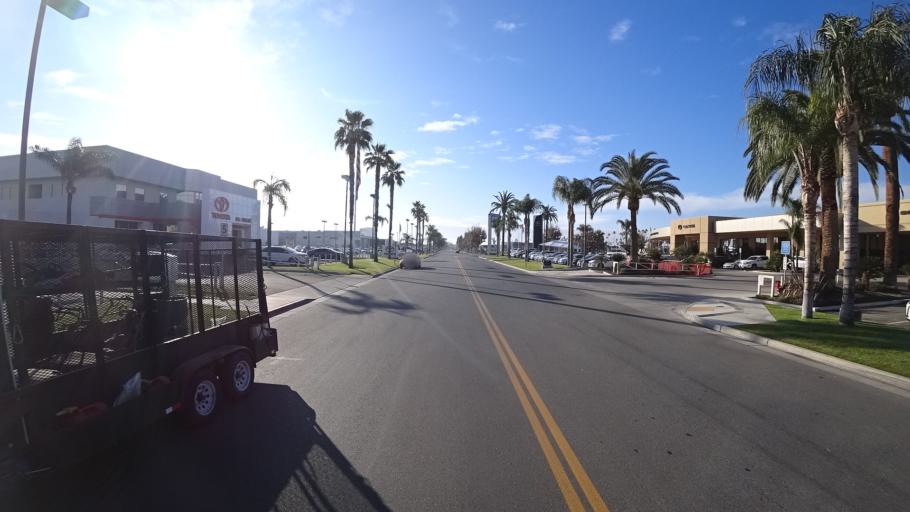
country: US
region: California
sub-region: Kern County
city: Greenfield
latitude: 35.3083
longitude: -119.0355
